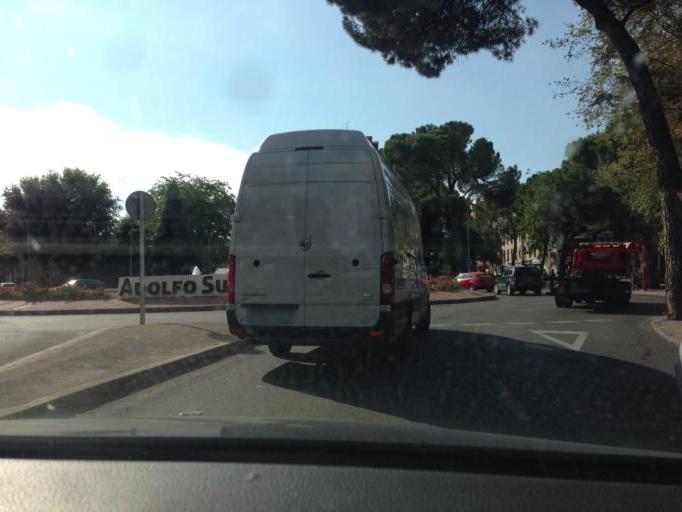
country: ES
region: Madrid
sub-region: Provincia de Madrid
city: Alcala de Henares
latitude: 40.4893
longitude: -3.3750
